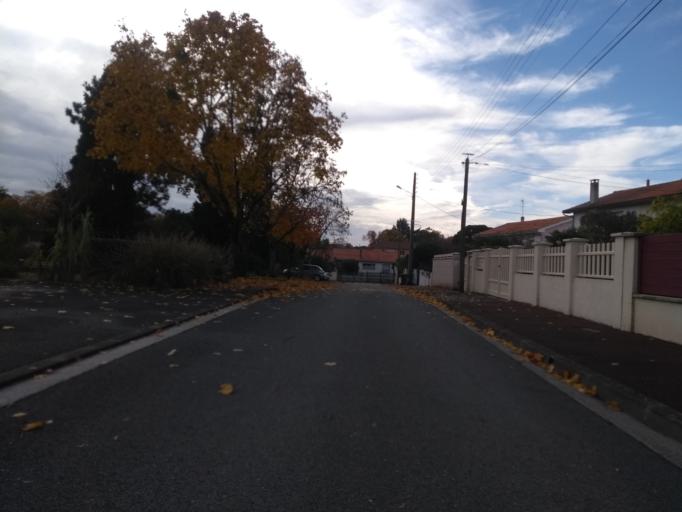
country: FR
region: Aquitaine
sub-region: Departement de la Gironde
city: Gradignan
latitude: 44.7780
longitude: -0.6187
